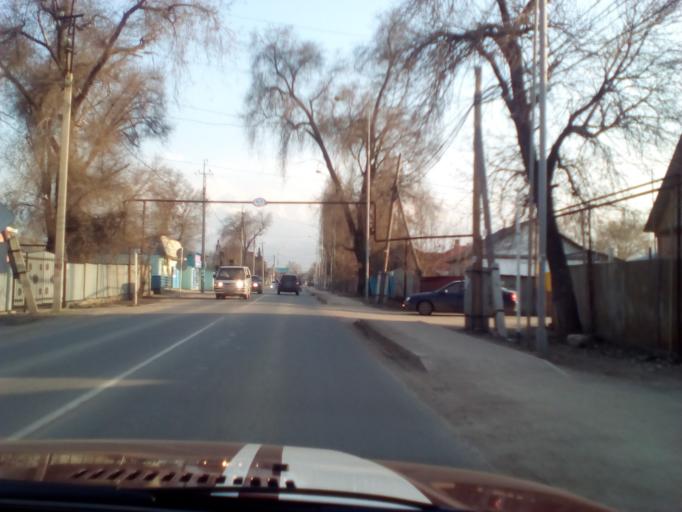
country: KZ
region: Almaty Oblysy
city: Burunday
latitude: 43.2562
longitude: 76.7688
